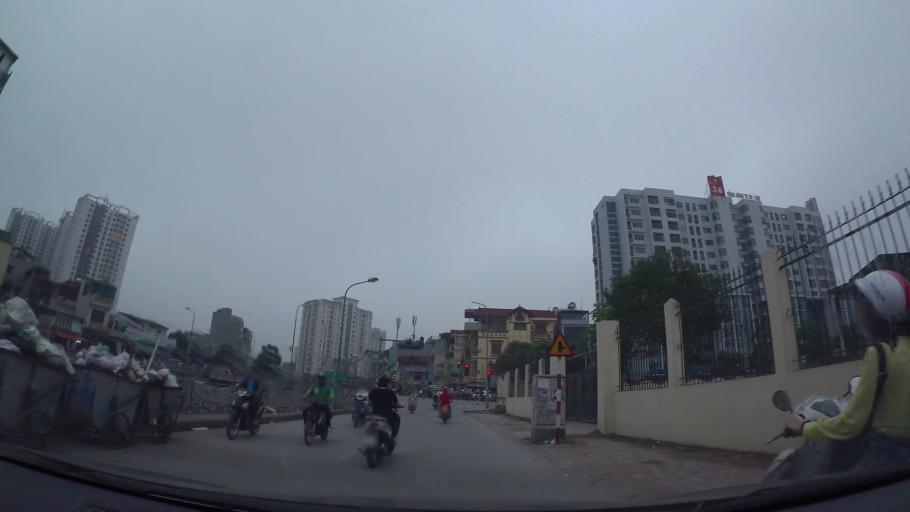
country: VN
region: Ha Noi
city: Hai BaTrung
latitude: 20.9875
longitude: 105.8361
